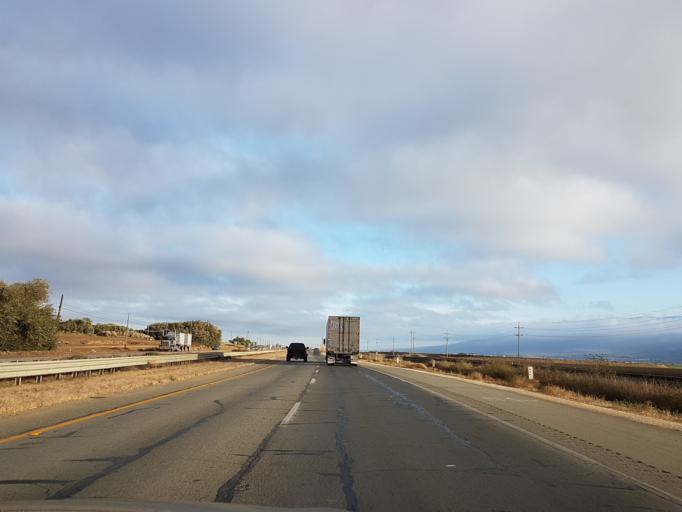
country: US
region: California
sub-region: Monterey County
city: Chualar
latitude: 36.5633
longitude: -121.5123
